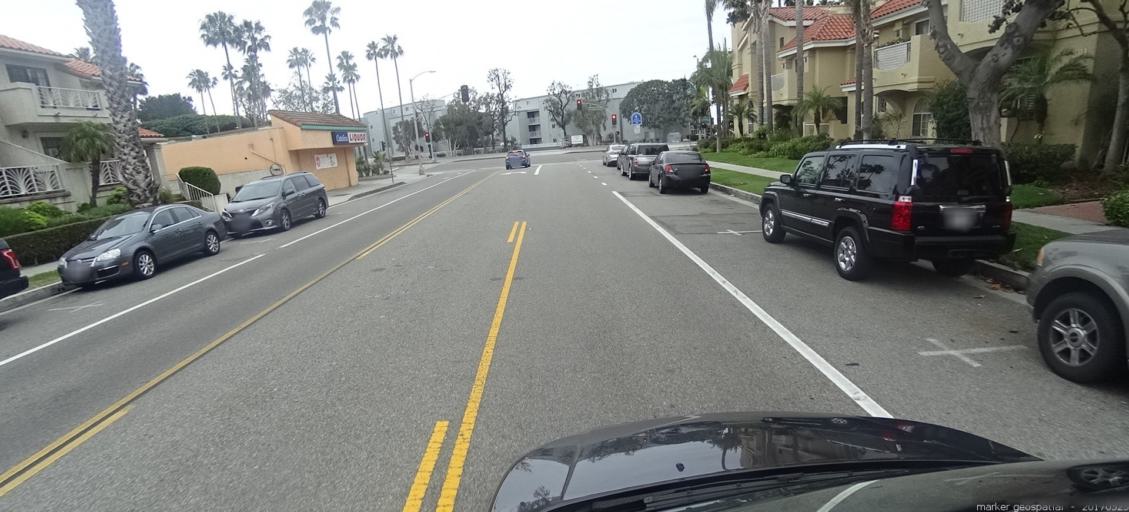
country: US
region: California
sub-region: Los Angeles County
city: Redondo Beach
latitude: 33.8438
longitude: -118.3888
